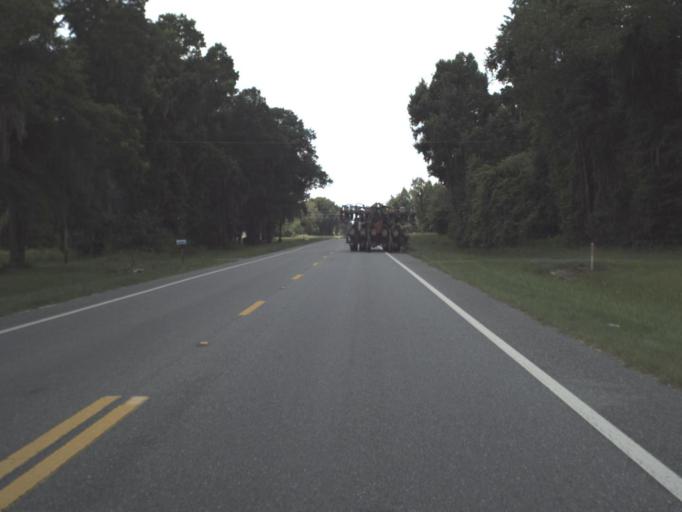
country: US
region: Florida
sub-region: Hamilton County
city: Jasper
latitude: 30.5380
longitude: -83.0490
